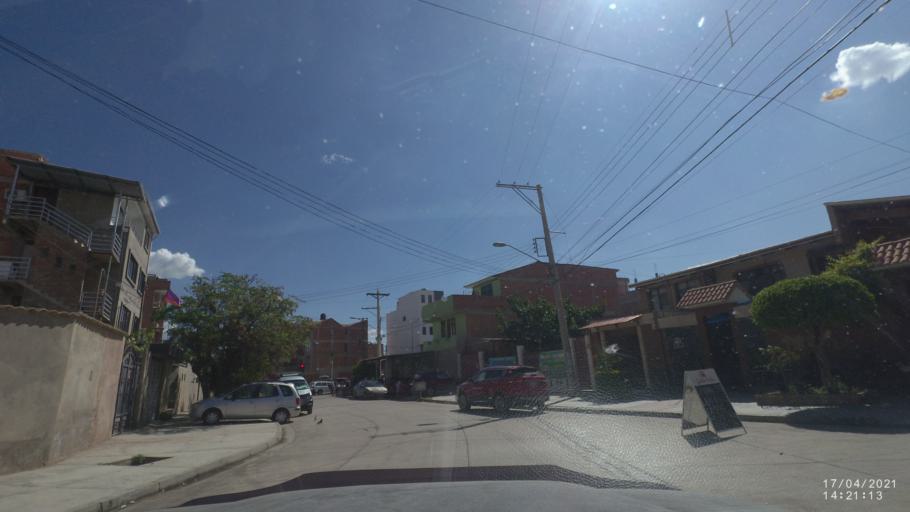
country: BO
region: Cochabamba
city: Cochabamba
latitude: -17.4155
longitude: -66.1680
